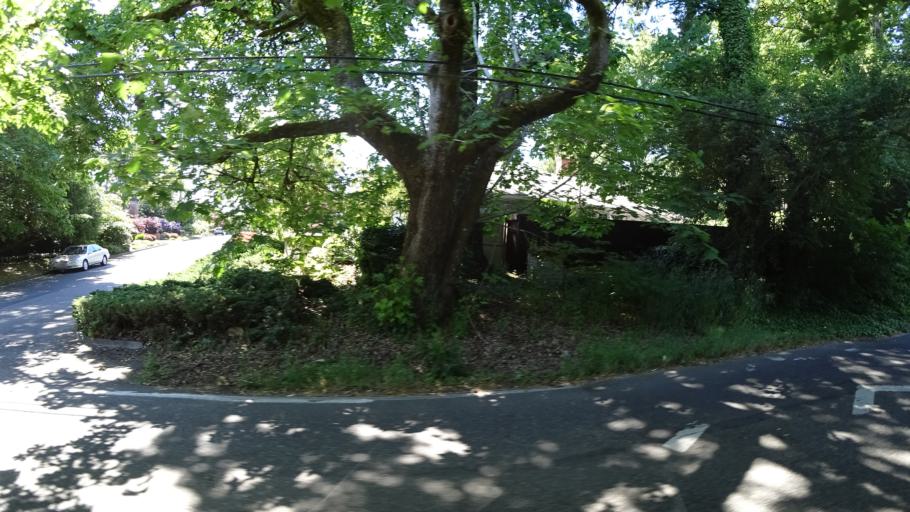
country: US
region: Oregon
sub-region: Washington County
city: Raleigh Hills
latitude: 45.4922
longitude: -122.7281
